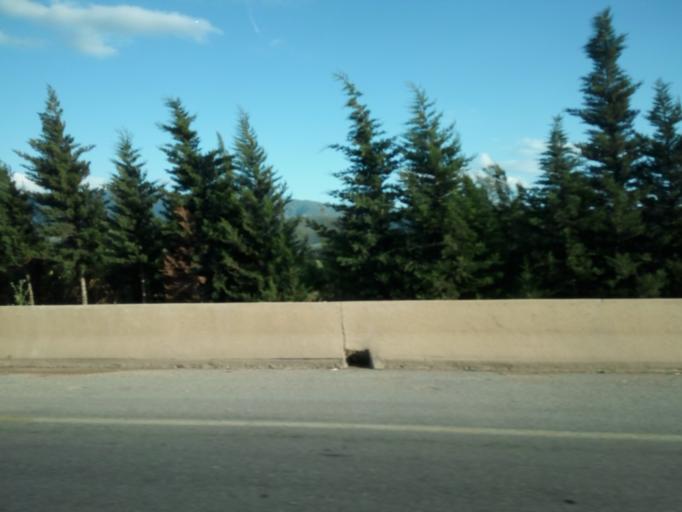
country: DZ
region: Tipaza
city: El Affroun
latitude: 36.4477
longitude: 2.6482
